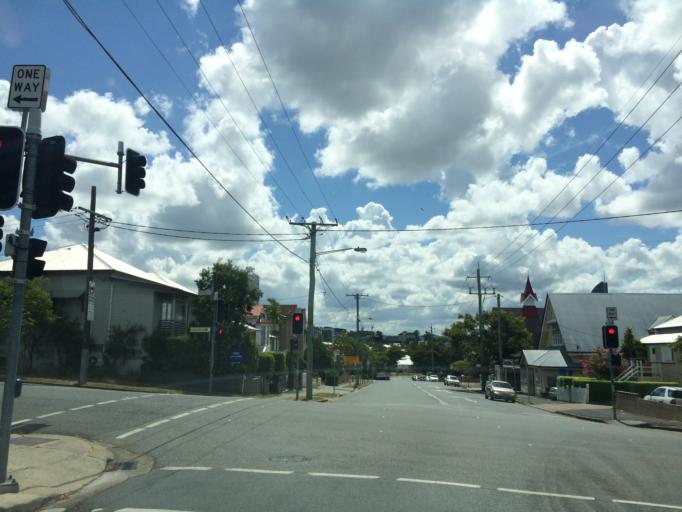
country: AU
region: Queensland
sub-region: Brisbane
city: Woolloongabba
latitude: -27.4835
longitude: 153.0434
